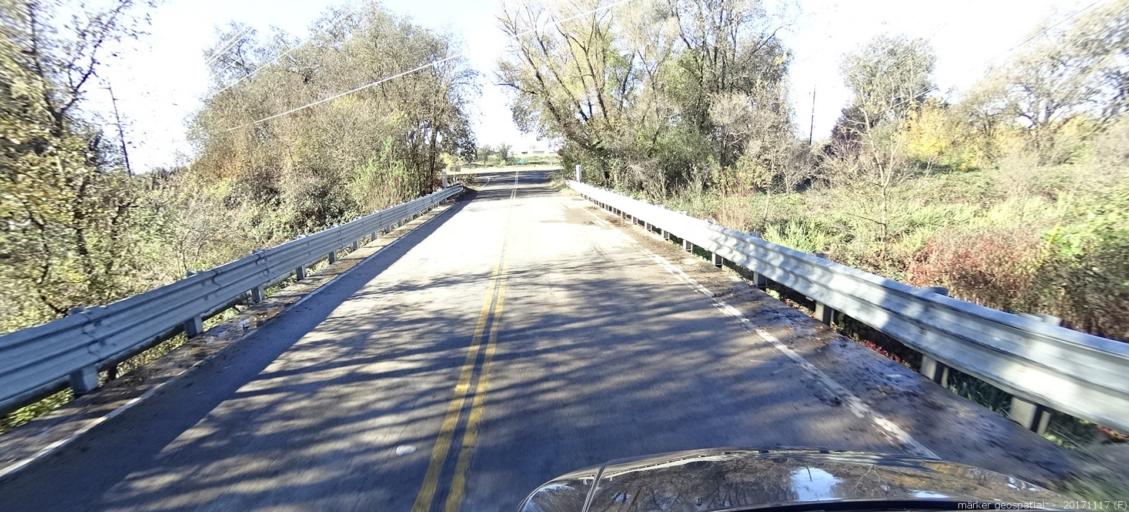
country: US
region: California
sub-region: Shasta County
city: Cottonwood
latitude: 40.4181
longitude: -122.2133
